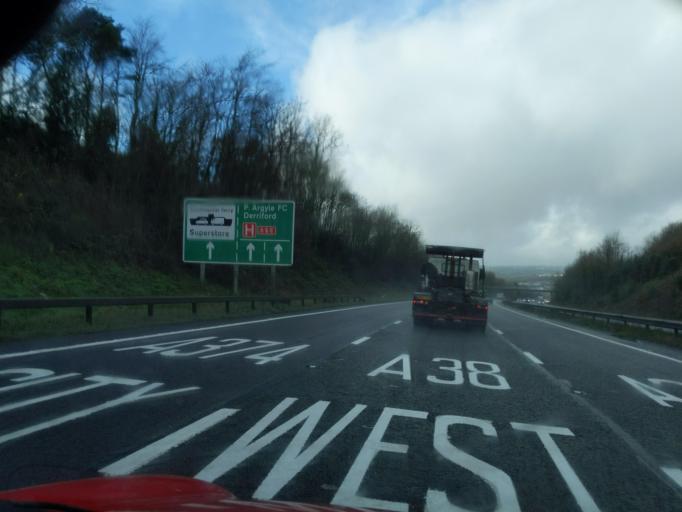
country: GB
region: England
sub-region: Devon
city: Plympton
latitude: 50.3808
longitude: -4.0752
